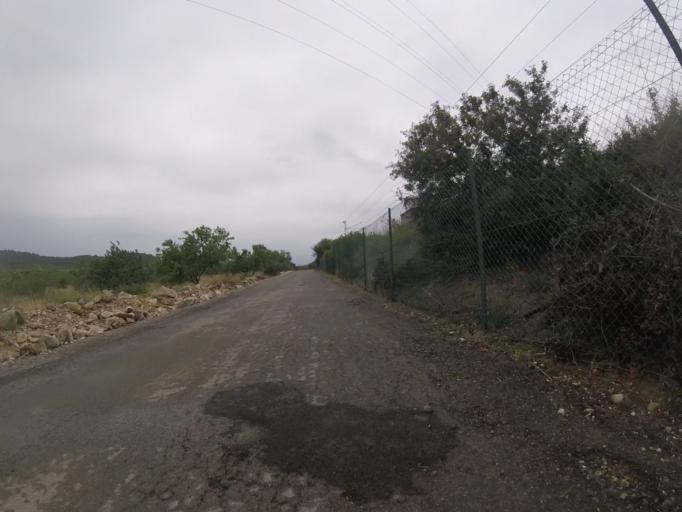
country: ES
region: Valencia
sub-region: Provincia de Castello
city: Alcala de Xivert
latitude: 40.2740
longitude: 0.2397
